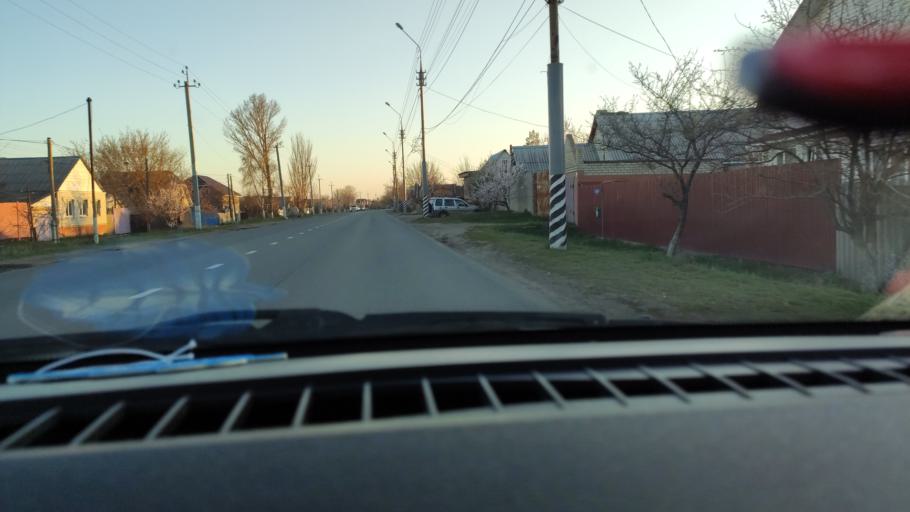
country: RU
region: Saratov
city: Privolzhskiy
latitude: 51.4286
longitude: 46.0517
